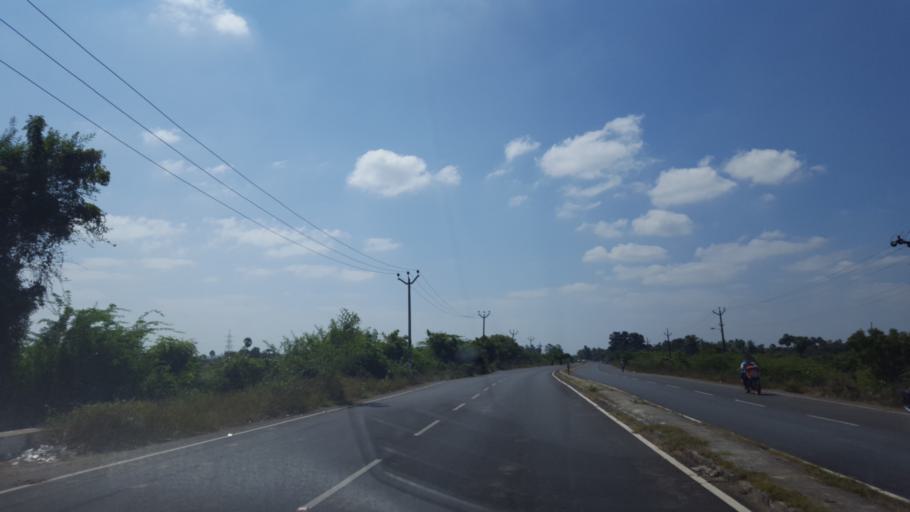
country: IN
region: Tamil Nadu
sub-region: Kancheepuram
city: Mamallapuram
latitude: 12.6882
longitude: 80.1799
